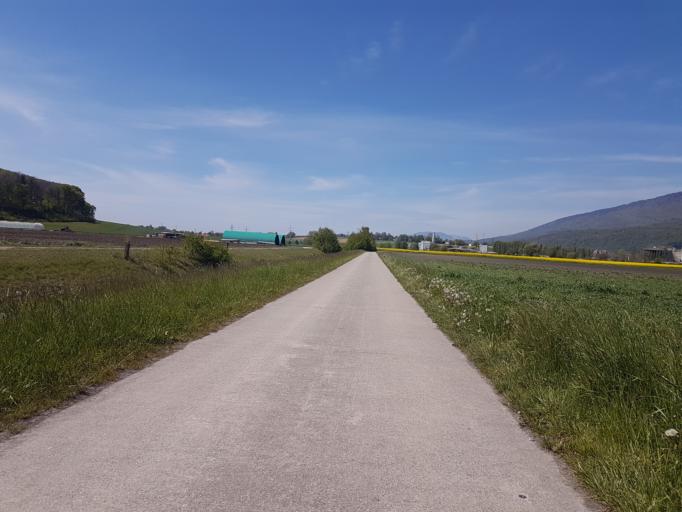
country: CH
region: Neuchatel
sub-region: Neuchatel District
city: Cornaux
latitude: 47.0342
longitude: 7.0436
